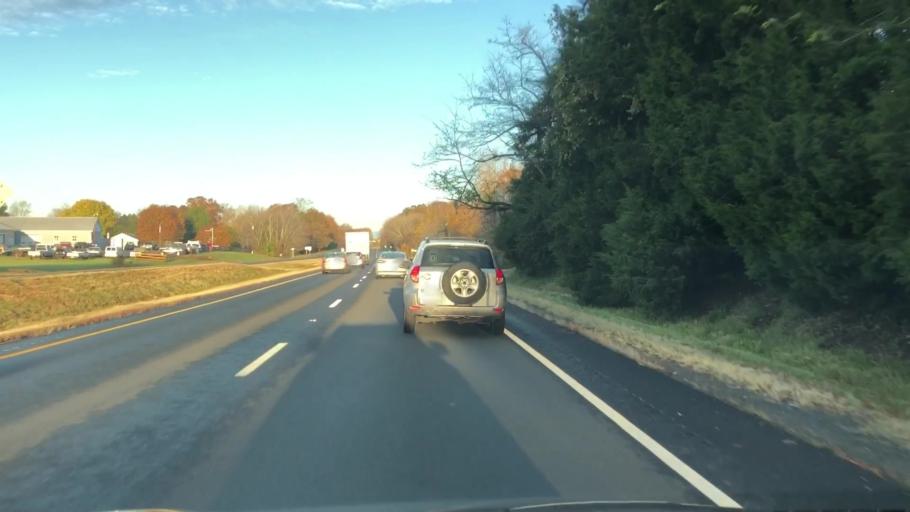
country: US
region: Virginia
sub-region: Fauquier County
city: Bealeton
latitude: 38.5020
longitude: -77.6955
